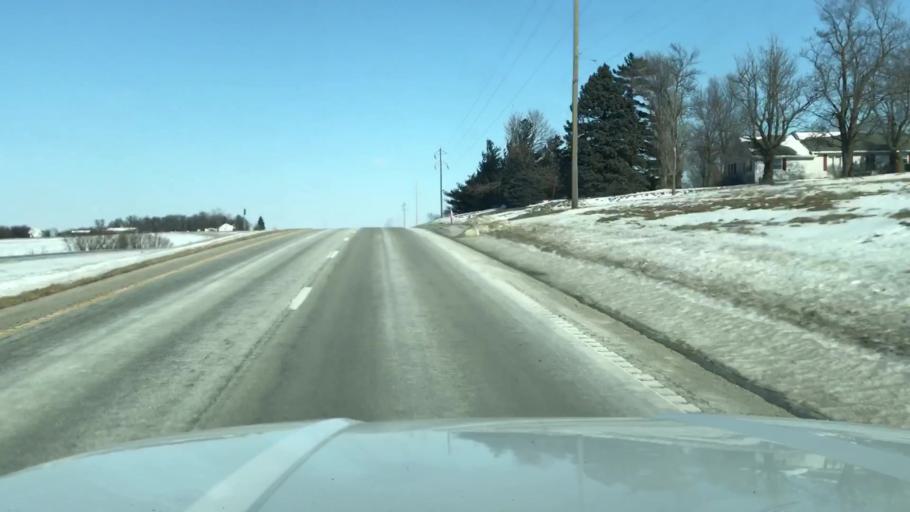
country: US
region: Missouri
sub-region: Nodaway County
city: Maryville
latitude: 40.1519
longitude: -94.8691
